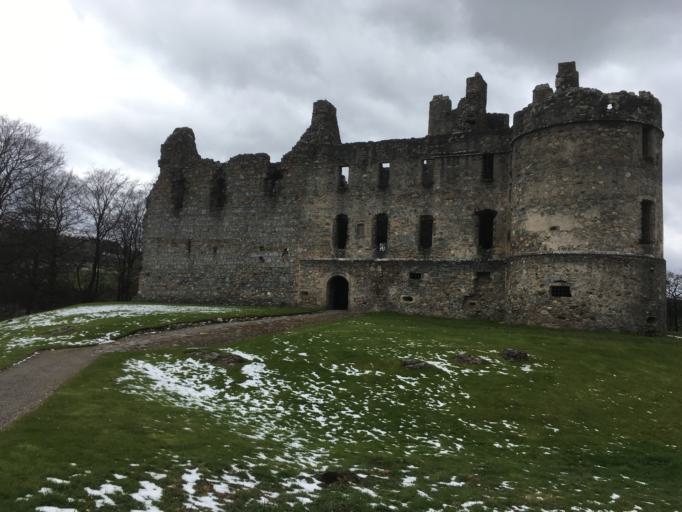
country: GB
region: Scotland
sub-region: Moray
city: Dufftown
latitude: 57.4531
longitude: -3.1238
